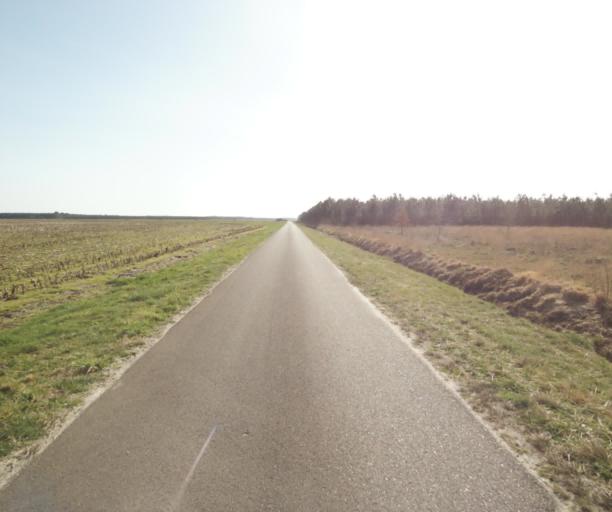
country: FR
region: Aquitaine
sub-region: Departement des Landes
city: Roquefort
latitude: 44.1782
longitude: -0.2520
